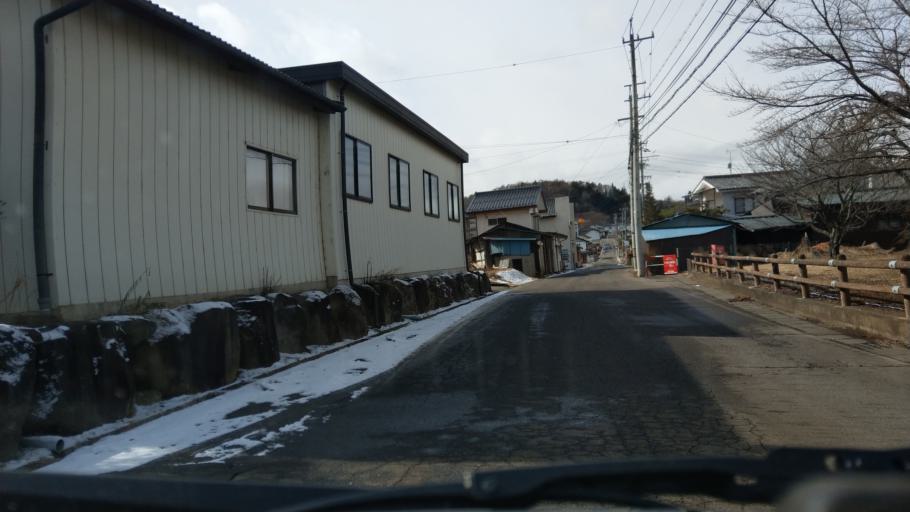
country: JP
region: Nagano
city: Kamimaruko
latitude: 36.2700
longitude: 138.3352
